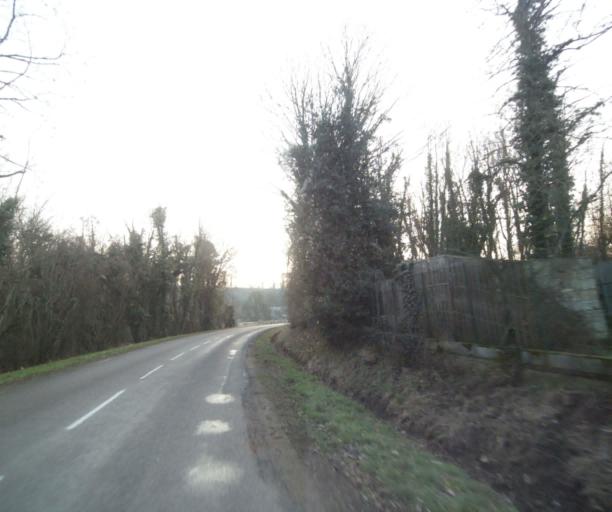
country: FR
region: Champagne-Ardenne
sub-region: Departement de la Haute-Marne
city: Bienville
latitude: 48.6095
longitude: 5.0559
